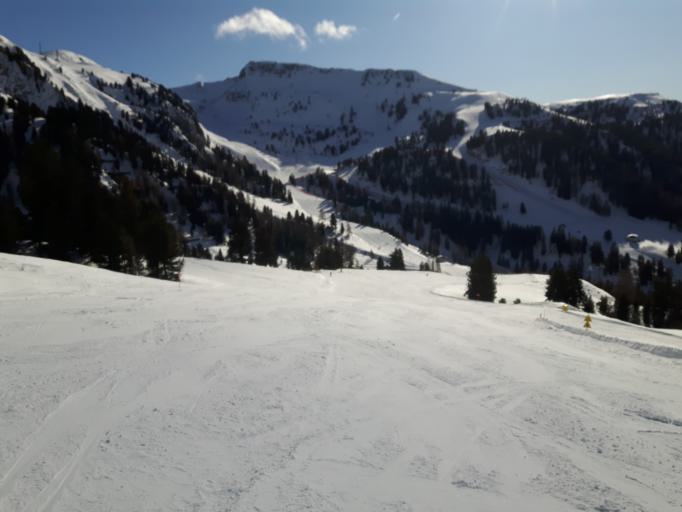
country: IT
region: Trentino-Alto Adige
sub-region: Provincia di Trento
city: Predazzo
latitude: 46.3477
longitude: 11.5511
